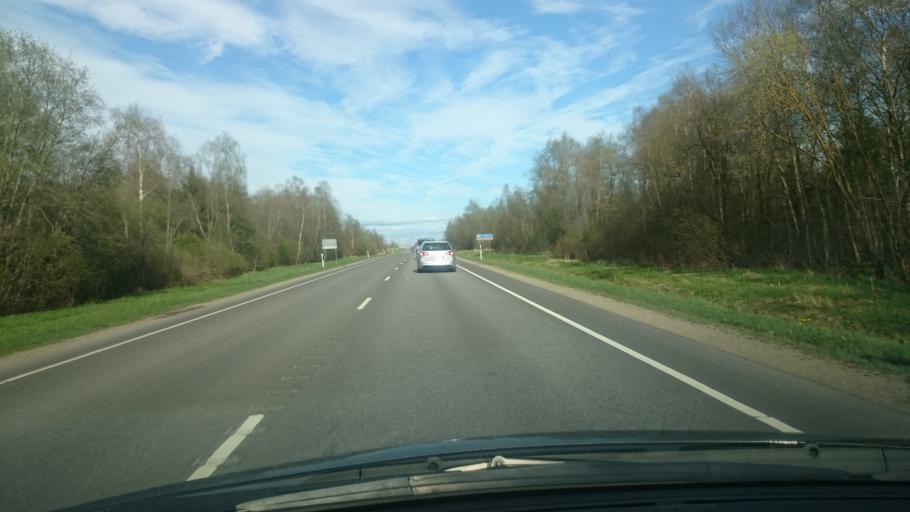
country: EE
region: Ida-Virumaa
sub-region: Sillamaee linn
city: Sillamae
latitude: 59.3914
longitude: 27.7115
